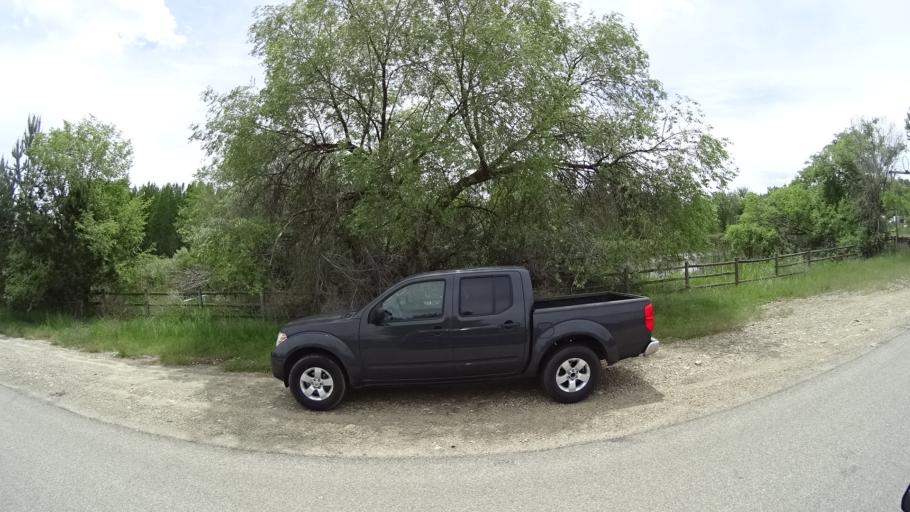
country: US
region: Idaho
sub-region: Ada County
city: Eagle
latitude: 43.6941
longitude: -116.4056
